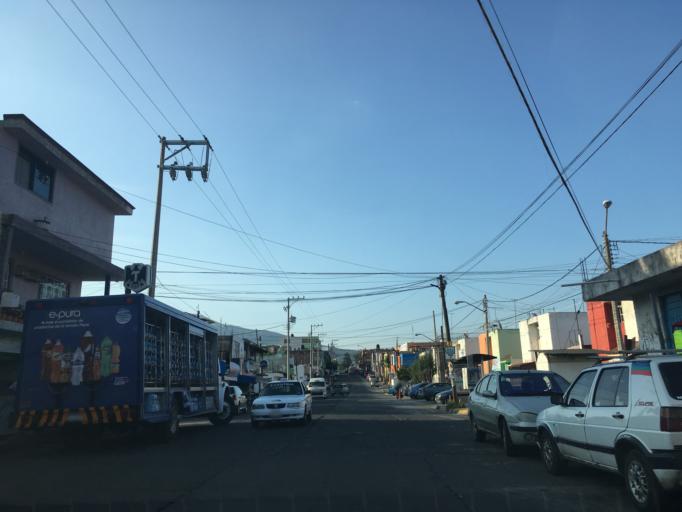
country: MX
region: Michoacan
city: Morelia
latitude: 19.6999
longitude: -101.2288
